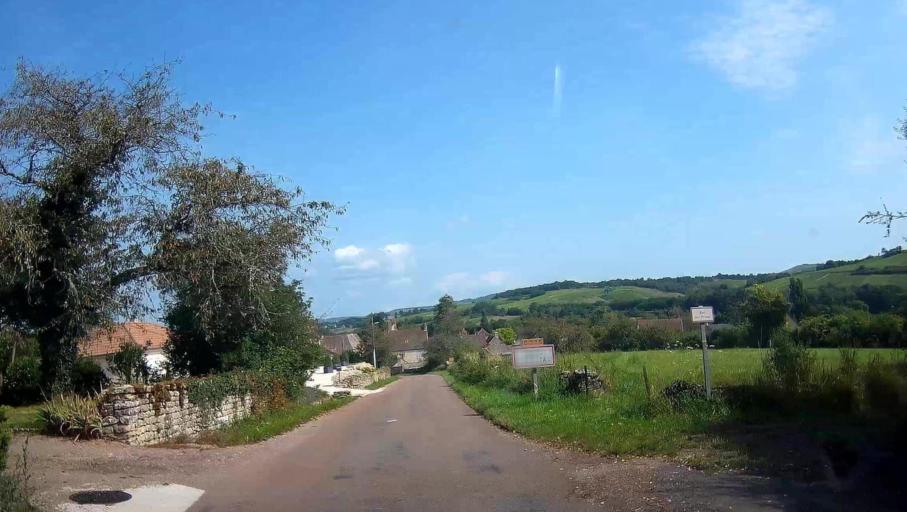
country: FR
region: Bourgogne
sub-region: Departement de la Cote-d'Or
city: Nolay
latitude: 46.9125
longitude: 4.6326
